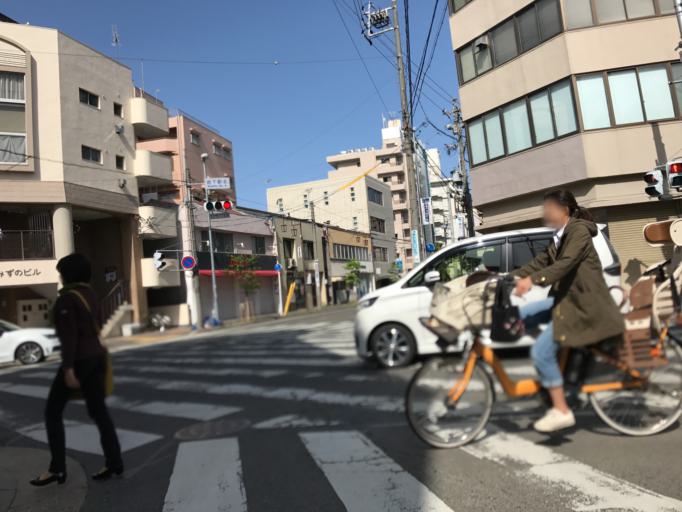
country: JP
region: Aichi
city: Nagoya-shi
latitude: 35.1690
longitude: 136.9459
